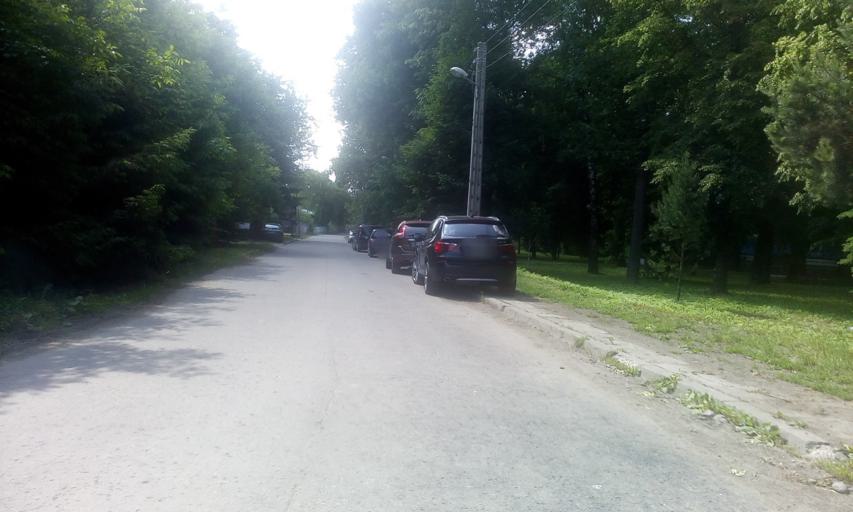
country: PL
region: Lesser Poland Voivodeship
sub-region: Powiat nowosadecki
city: Nowy Sacz
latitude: 49.6165
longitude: 20.6860
